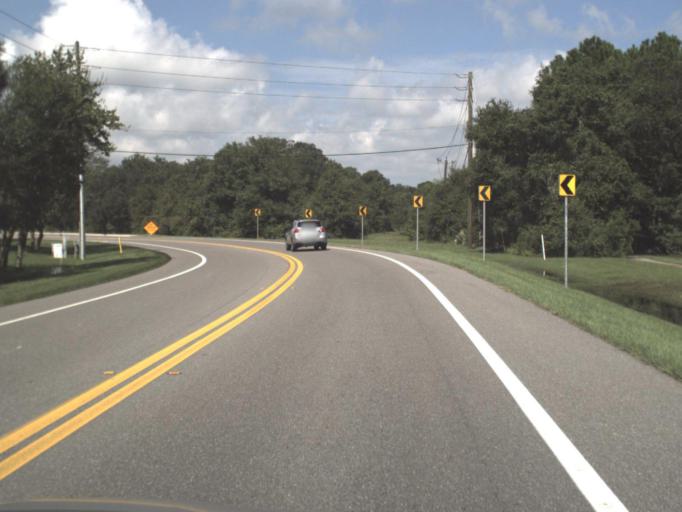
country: US
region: Florida
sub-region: Sarasota County
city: Lake Sarasota
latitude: 27.2687
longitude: -82.4189
